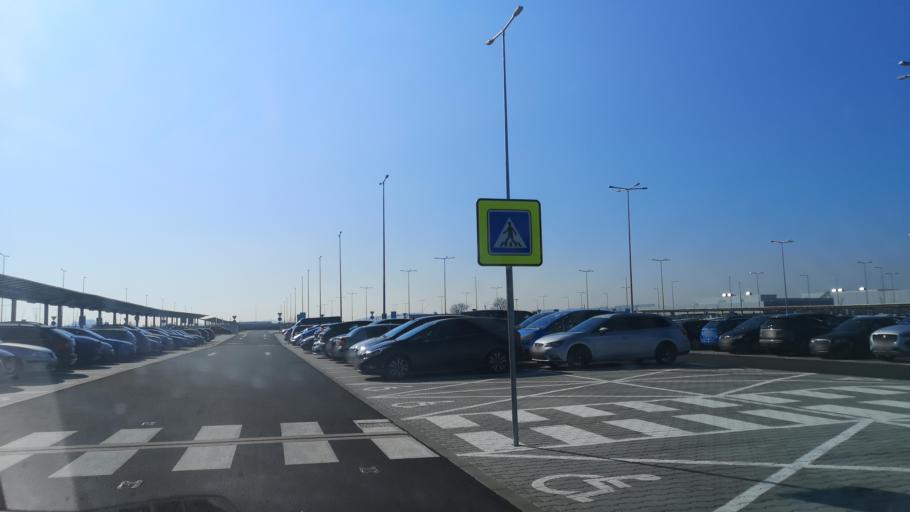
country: SK
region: Nitriansky
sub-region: Okres Nitra
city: Nitra
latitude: 48.3471
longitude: 18.0519
